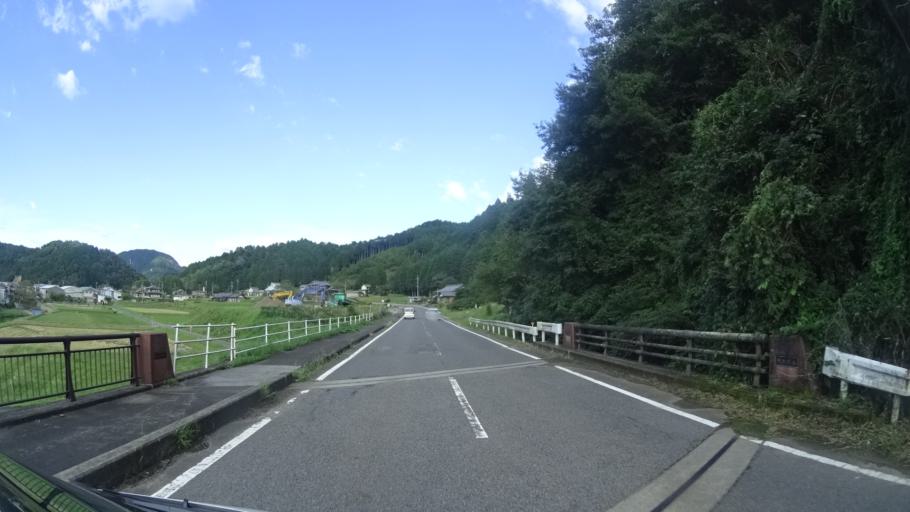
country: JP
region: Gifu
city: Minokamo
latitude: 35.5728
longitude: 137.0868
